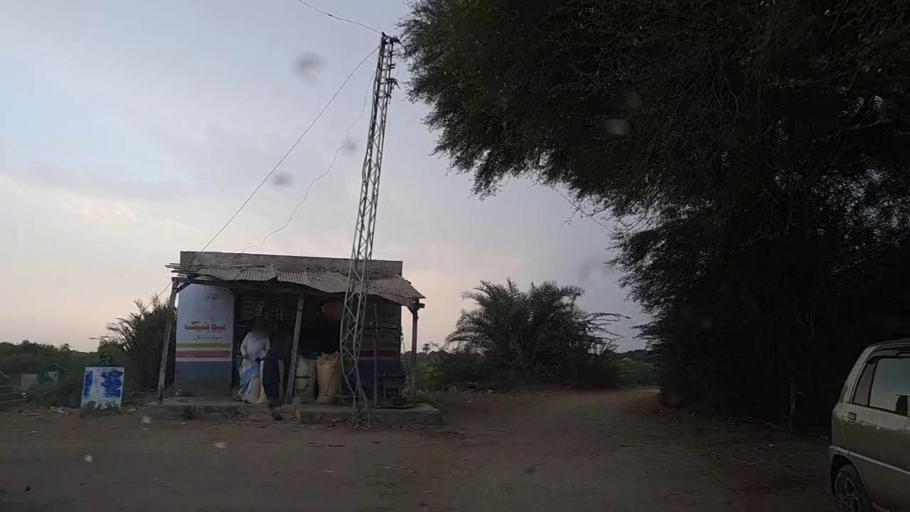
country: PK
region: Sindh
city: Daro Mehar
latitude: 24.7920
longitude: 68.1771
